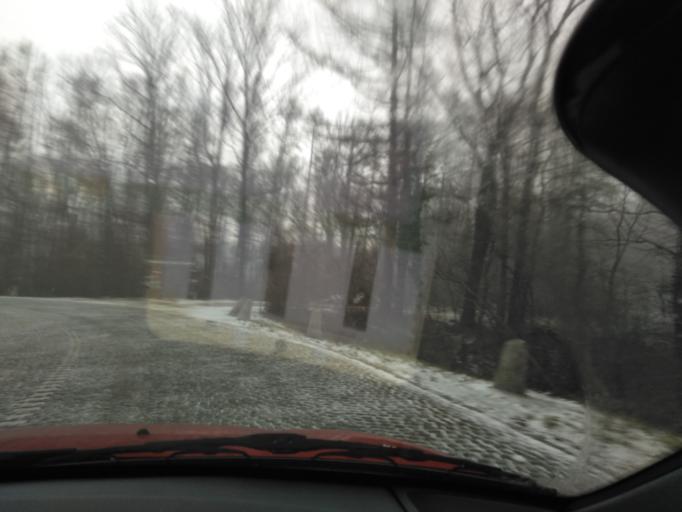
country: AT
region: Lower Austria
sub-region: Politischer Bezirk Wien-Umgebung
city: Klosterneuburg
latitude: 48.2583
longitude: 16.2919
